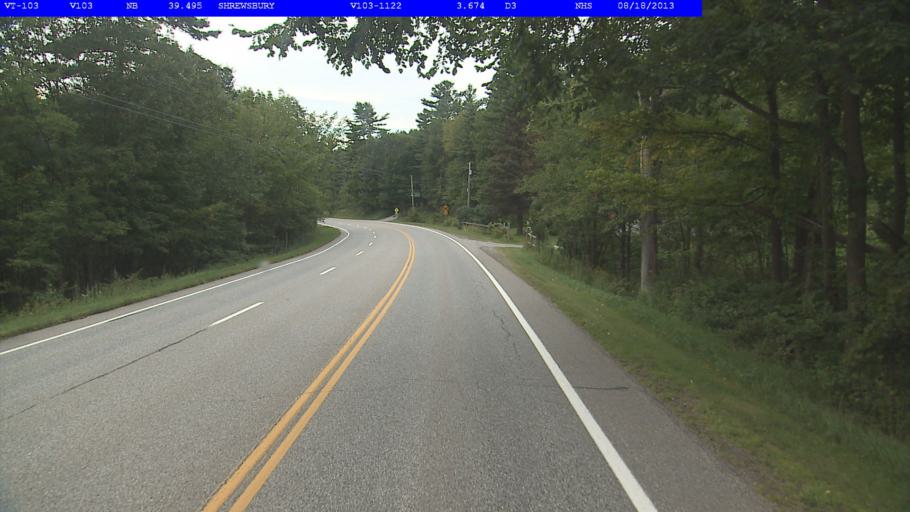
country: US
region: Vermont
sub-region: Rutland County
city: Rutland
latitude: 43.5196
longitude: -72.9218
